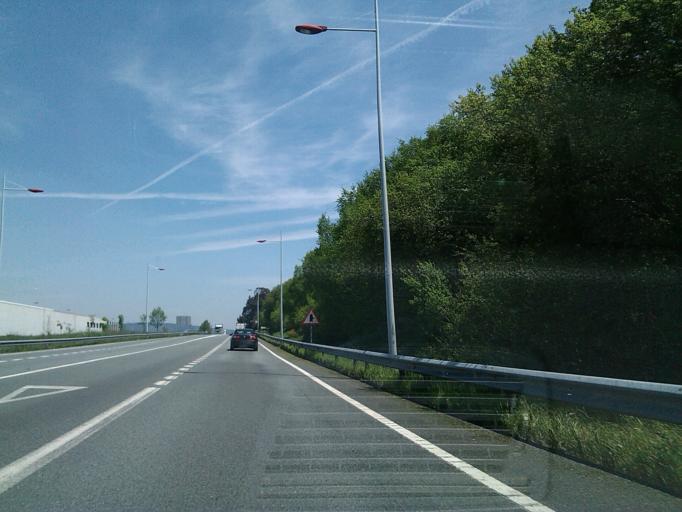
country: ES
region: Galicia
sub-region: Provincia da Coruna
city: Curtis
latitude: 43.1483
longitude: -8.0159
